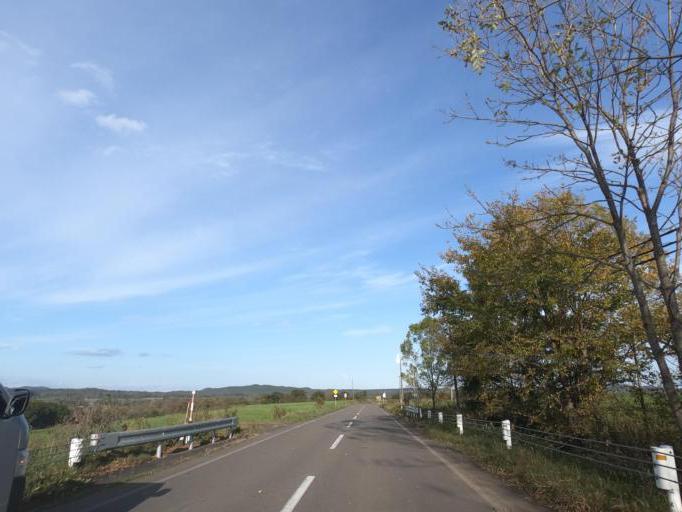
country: JP
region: Hokkaido
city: Obihiro
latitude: 42.5607
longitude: 143.3431
